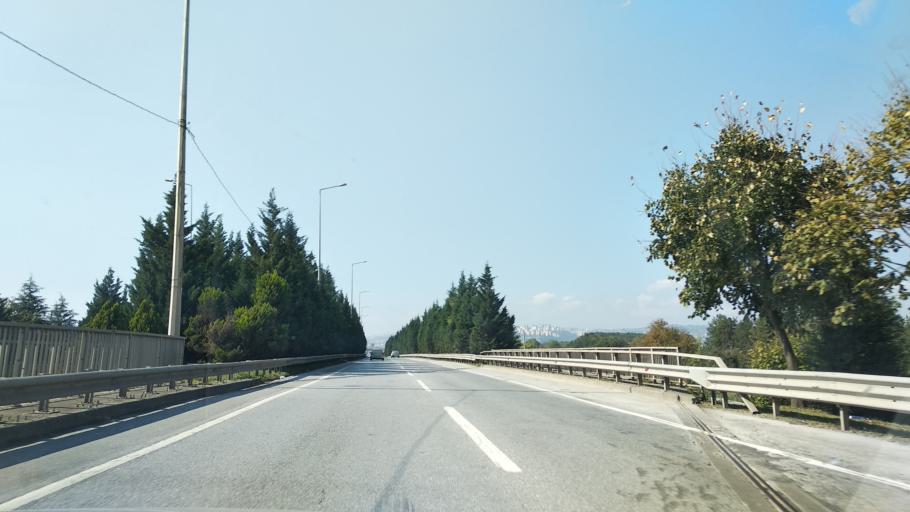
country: TR
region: Kocaeli
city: Kosekoy
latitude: 40.7556
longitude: 30.0090
